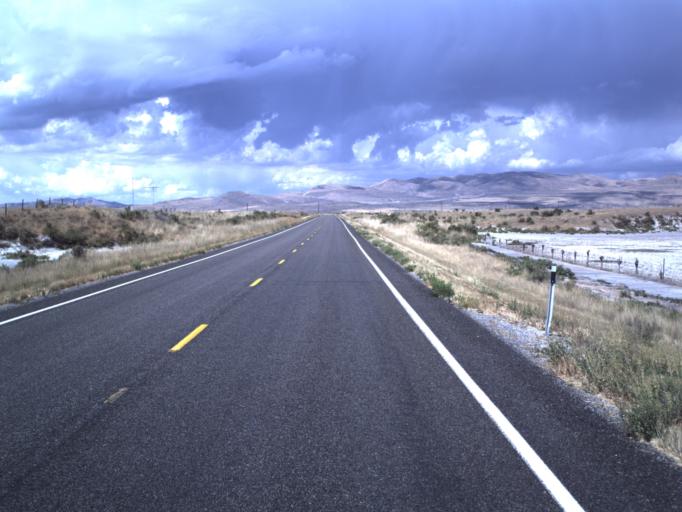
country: US
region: Utah
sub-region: Box Elder County
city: Tremonton
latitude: 41.5860
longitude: -112.2650
